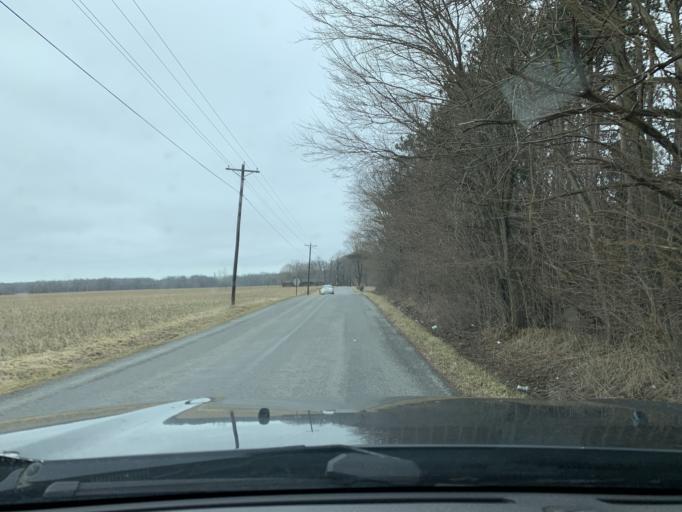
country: US
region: Indiana
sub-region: Porter County
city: Chesterton
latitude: 41.6044
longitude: -86.9899
